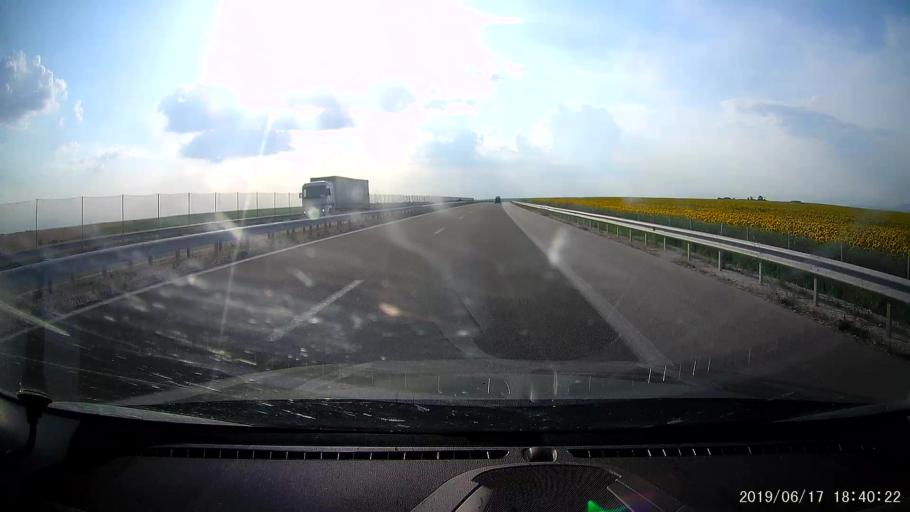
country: BG
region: Stara Zagora
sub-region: Obshtina Chirpan
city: Chirpan
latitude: 42.1546
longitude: 25.2798
